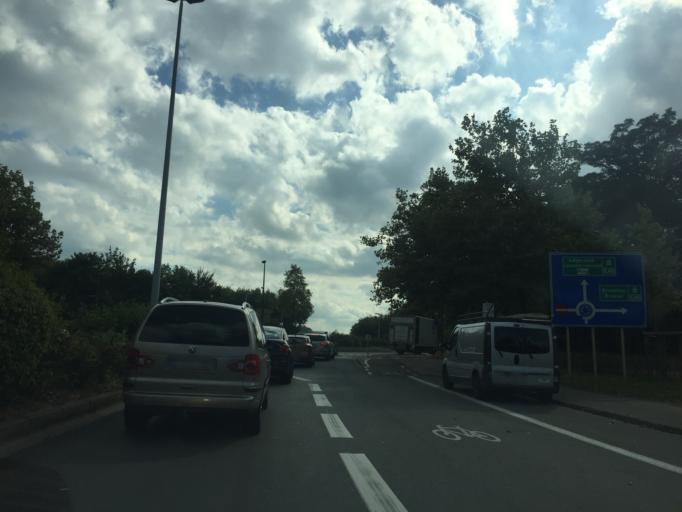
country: BE
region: Flanders
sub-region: Provincie Vlaams-Brabant
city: Diegem
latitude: 50.8589
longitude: 4.4246
